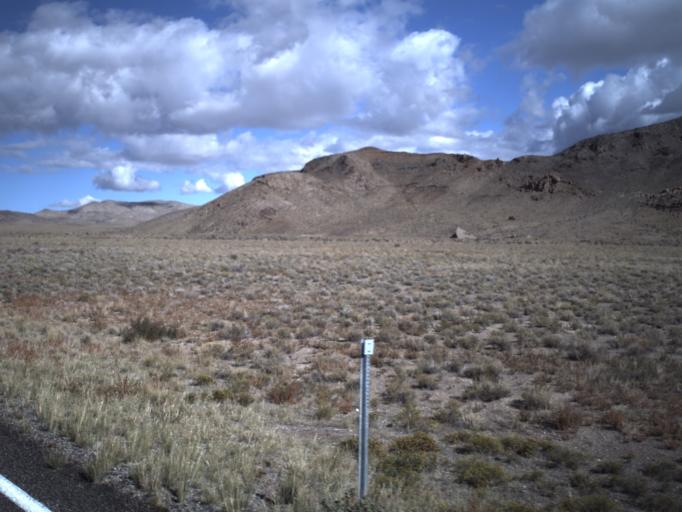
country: US
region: Utah
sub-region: Beaver County
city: Milford
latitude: 38.5808
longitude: -113.8082
